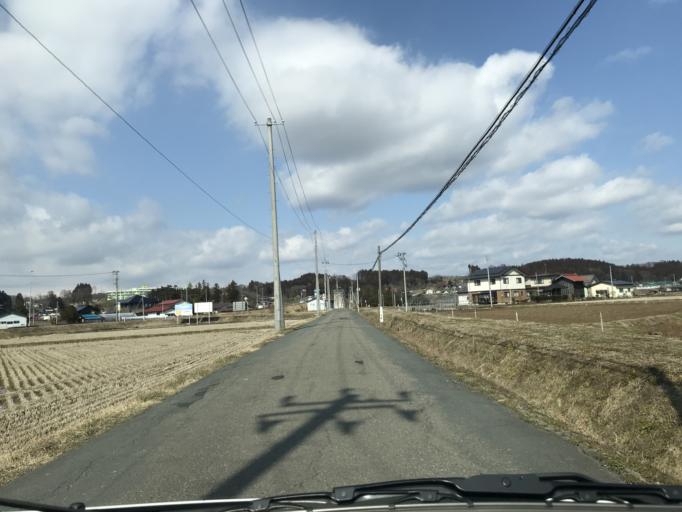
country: JP
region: Iwate
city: Mizusawa
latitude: 39.0663
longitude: 141.1360
